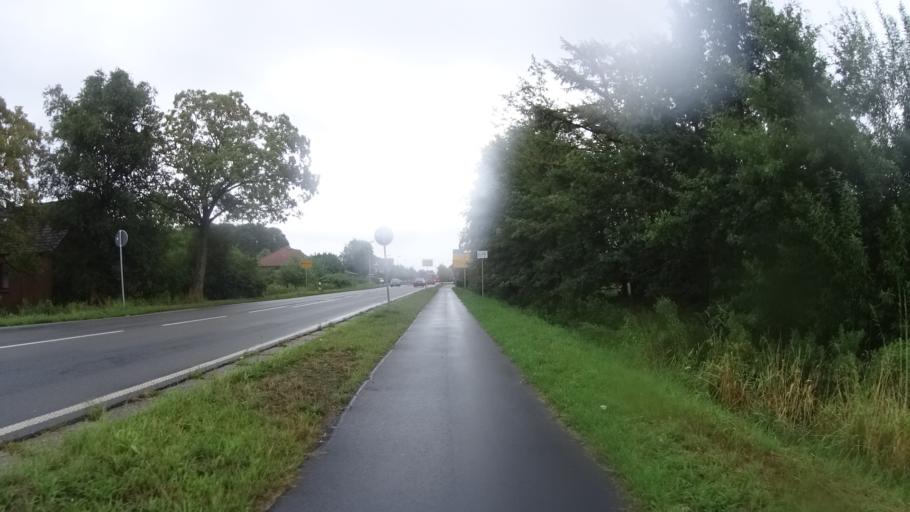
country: DE
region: Lower Saxony
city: Bunde
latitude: 53.1773
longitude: 7.2994
